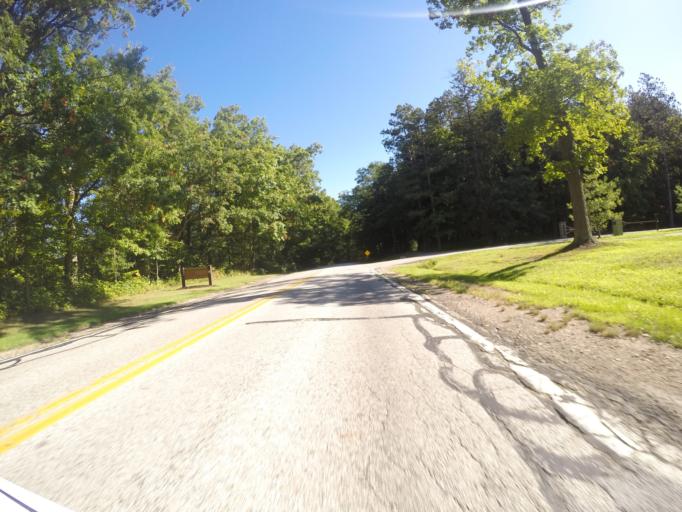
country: US
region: Ohio
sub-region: Cuyahoga County
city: Brecksville
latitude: 41.3097
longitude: -81.6042
